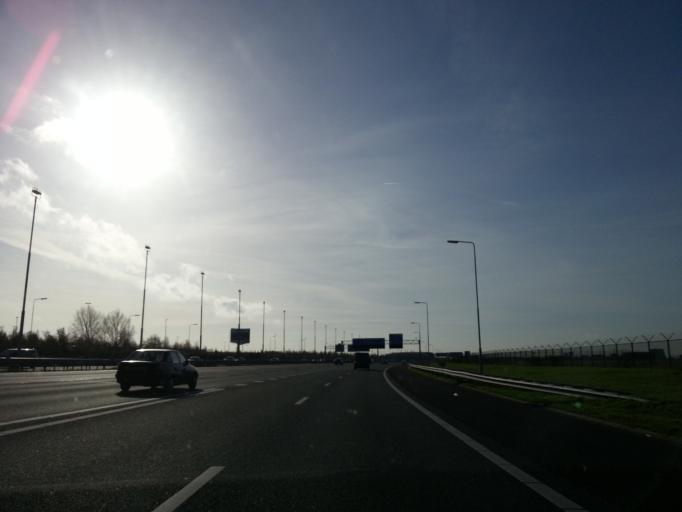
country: NL
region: North Holland
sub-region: Gemeente Aalsmeer
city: Aalsmeer
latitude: 52.3009
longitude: 4.7429
